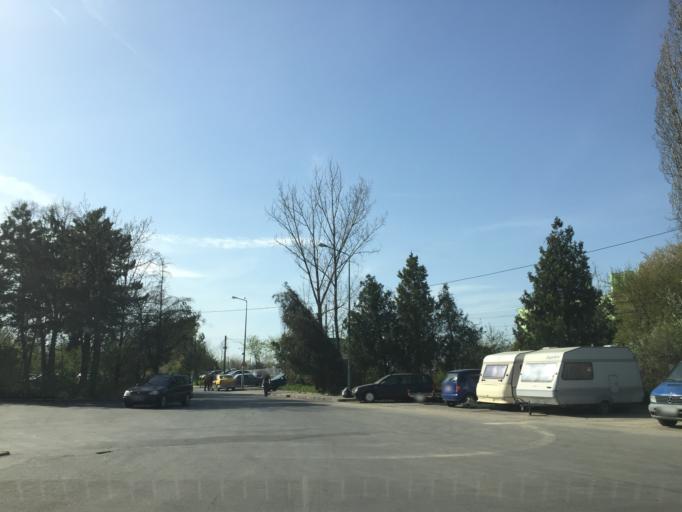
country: RO
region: Ilfov
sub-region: Comuna Popesti-Leordeni
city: Popesti-Leordeni
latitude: 44.3914
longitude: 26.1454
